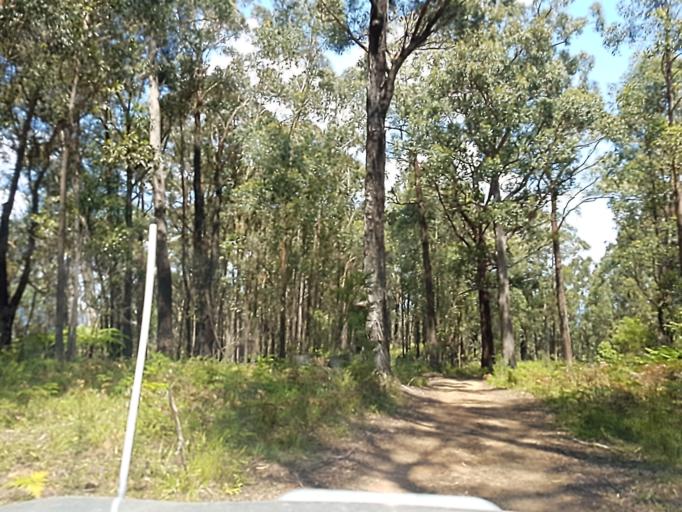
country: AU
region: Victoria
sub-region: East Gippsland
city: Lakes Entrance
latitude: -37.3930
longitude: 148.2956
